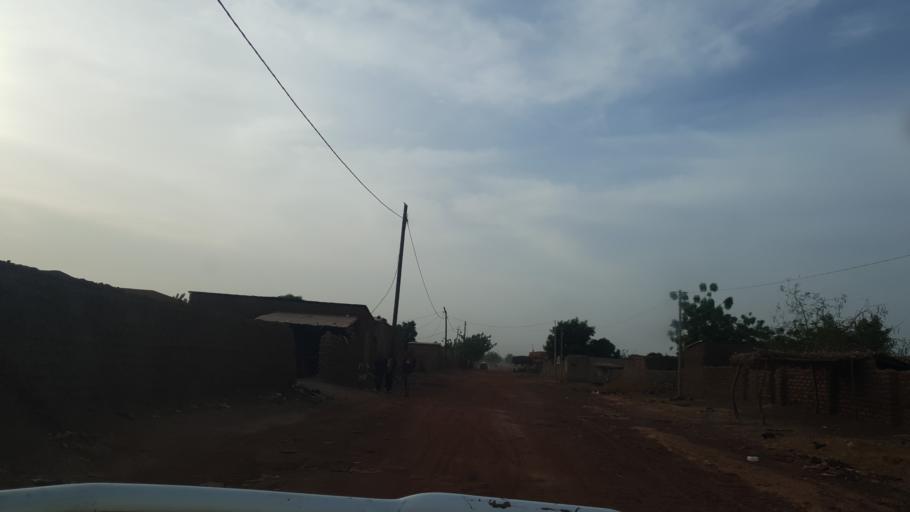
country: ML
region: Segou
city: Baroueli
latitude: 12.7843
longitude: -6.9453
